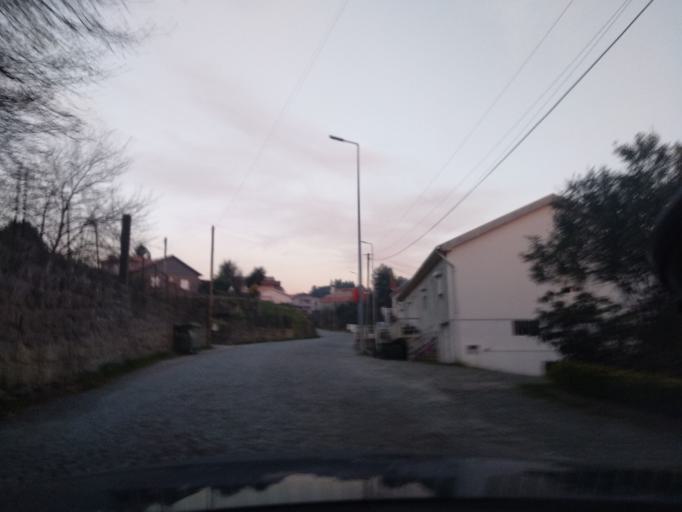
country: PT
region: Porto
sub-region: Paredes
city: Lordelo
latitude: 41.2341
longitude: -8.4022
